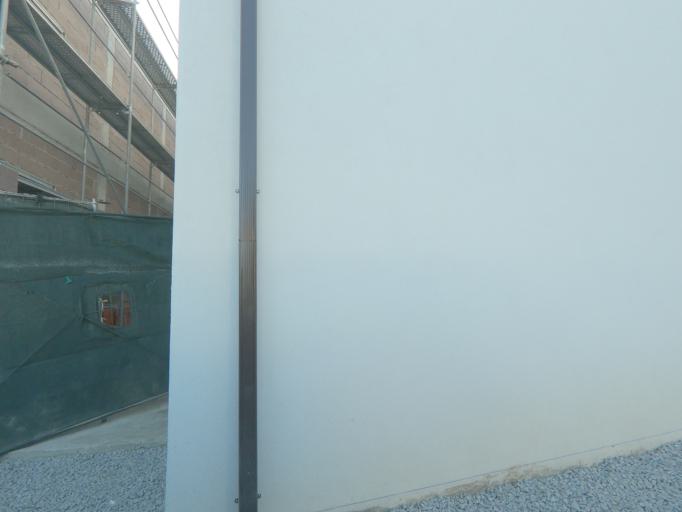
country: PT
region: Vila Real
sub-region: Peso da Regua
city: Godim
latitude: 41.1636
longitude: -7.8202
